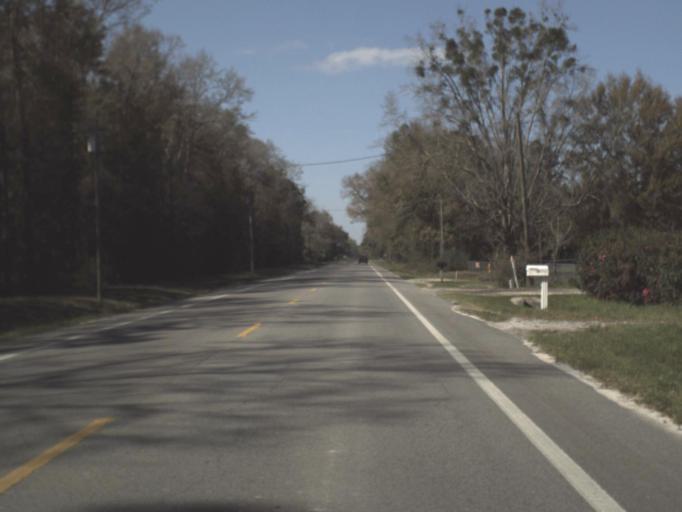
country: US
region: Florida
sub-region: Gulf County
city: Wewahitchka
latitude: 30.0529
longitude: -85.1881
